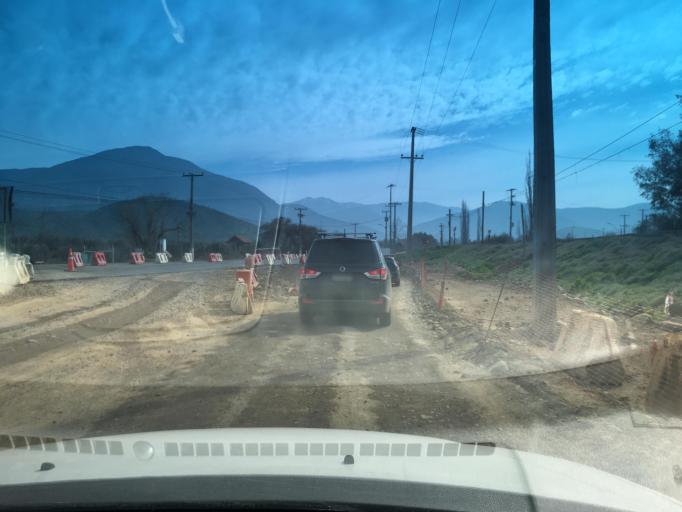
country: CL
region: Santiago Metropolitan
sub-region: Provincia de Chacabuco
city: Lampa
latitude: -33.1035
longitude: -70.9298
